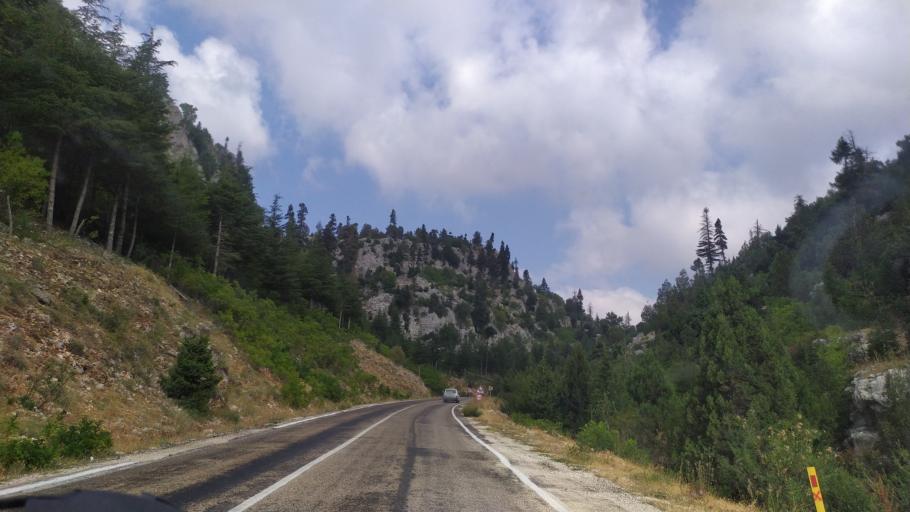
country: TR
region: Mersin
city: Kirobasi
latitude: 36.6036
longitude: 33.8879
